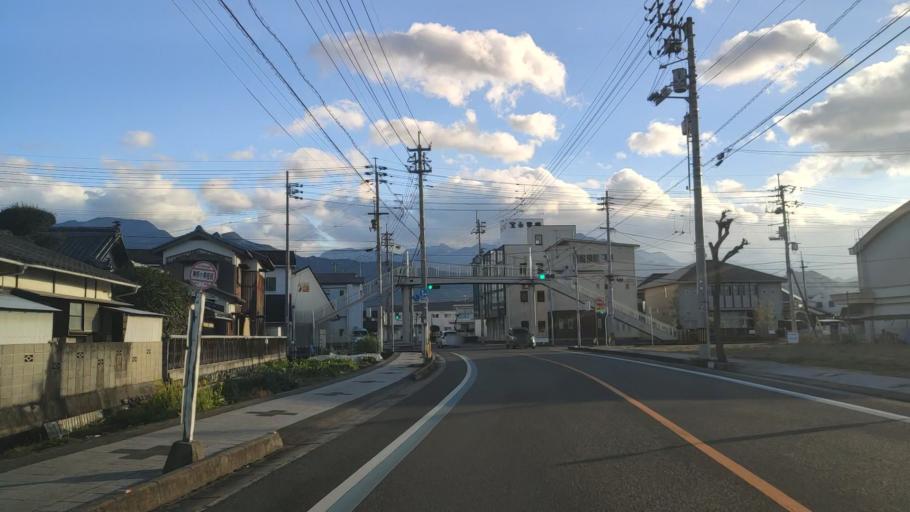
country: JP
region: Ehime
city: Saijo
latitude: 33.9151
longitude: 133.1778
